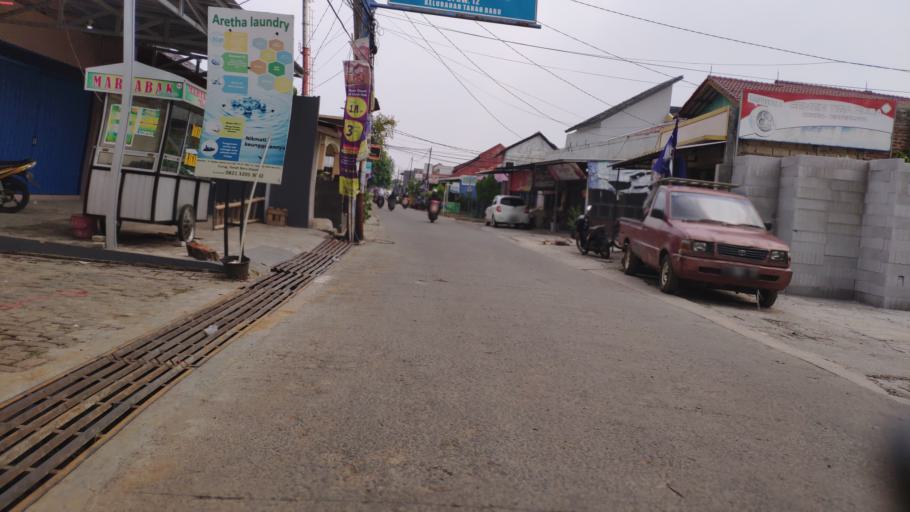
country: ID
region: West Java
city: Depok
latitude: -6.3748
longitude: 106.8011
